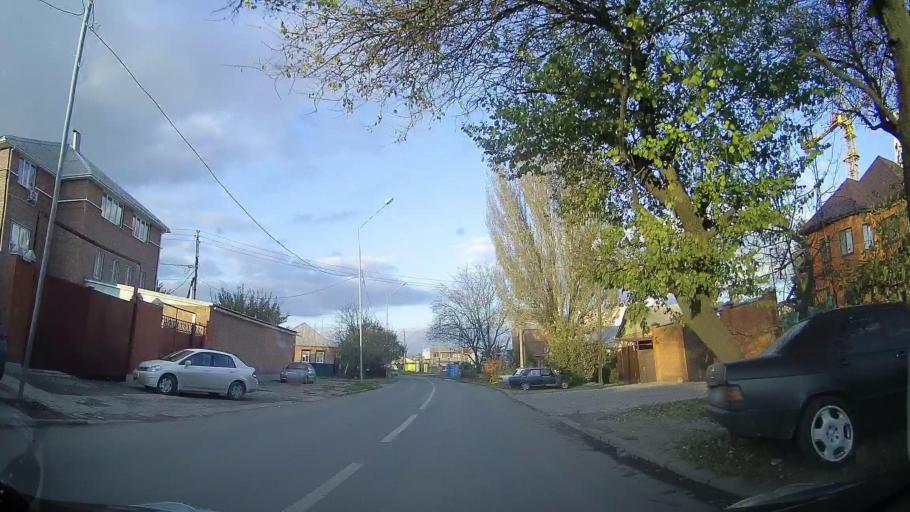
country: RU
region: Rostov
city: Imeni Chkalova
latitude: 47.2402
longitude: 39.7766
